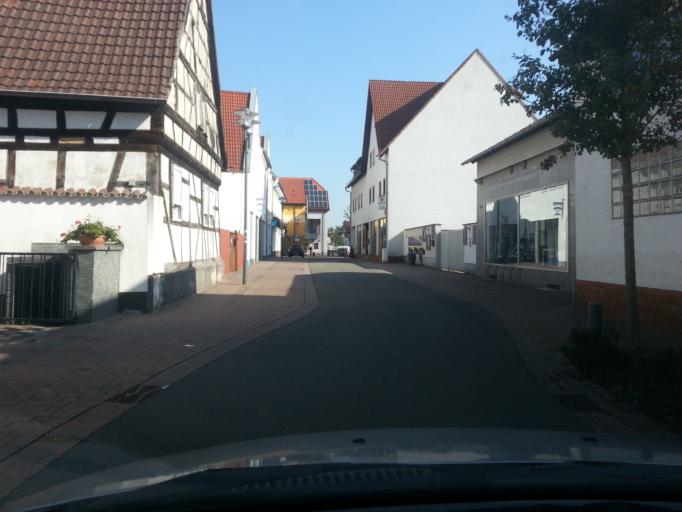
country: DE
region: Rheinland-Pfalz
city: Schifferstadt
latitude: 49.3865
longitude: 8.3723
